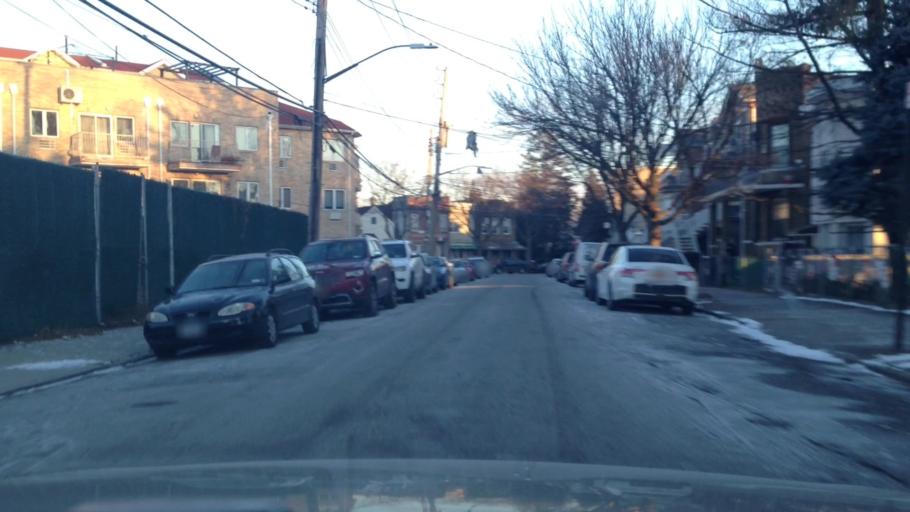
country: US
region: New York
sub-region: Kings County
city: Coney Island
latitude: 40.5854
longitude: -73.9861
